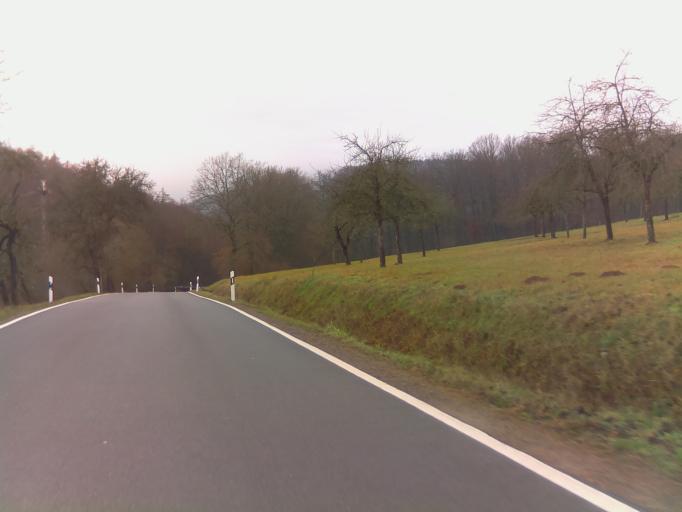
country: DE
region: Bavaria
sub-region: Regierungsbezirk Unterfranken
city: Schonau
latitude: 50.0740
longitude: 9.7354
